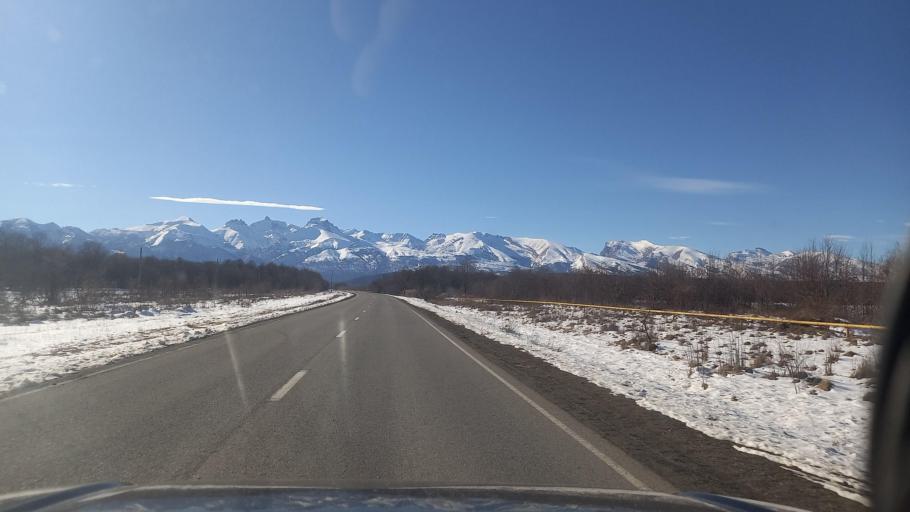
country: RU
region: North Ossetia
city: Chikola
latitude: 43.1645
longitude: 43.8563
